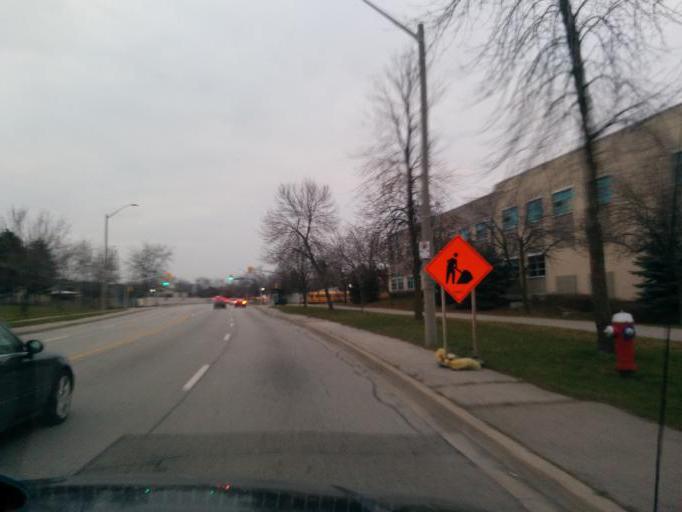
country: CA
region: Ontario
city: Mississauga
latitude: 43.6132
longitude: -79.6196
